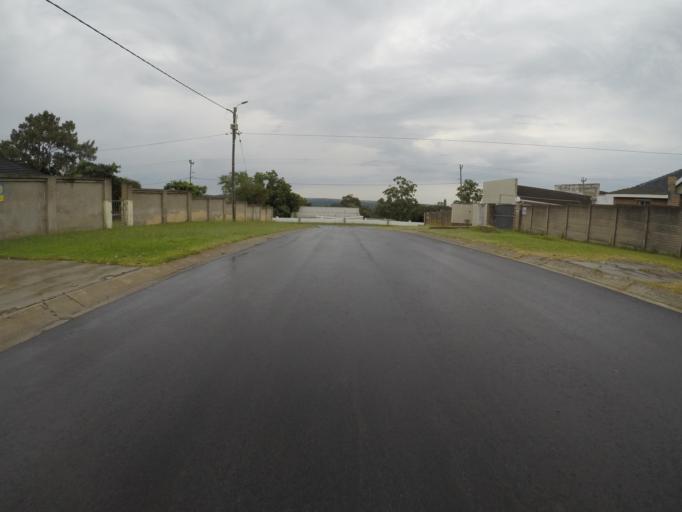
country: ZA
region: Eastern Cape
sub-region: Buffalo City Metropolitan Municipality
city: East London
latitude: -32.9668
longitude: 27.8463
